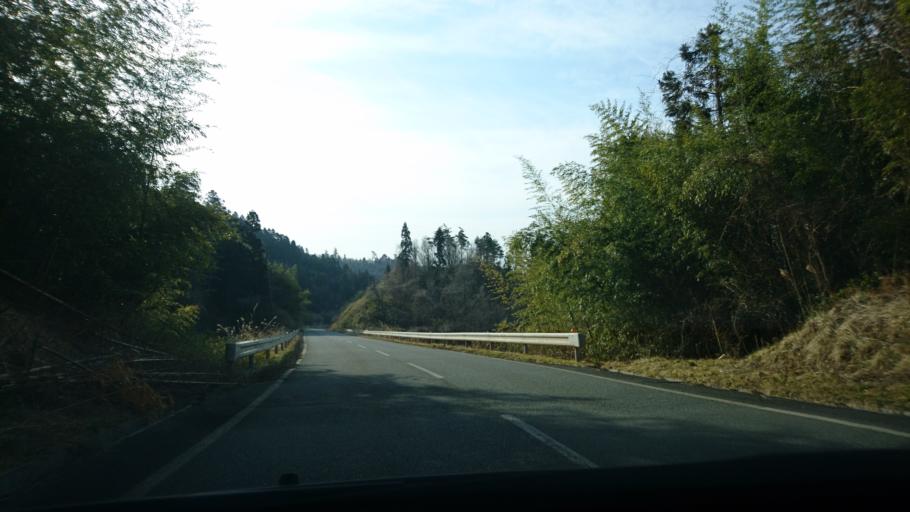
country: JP
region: Iwate
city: Ichinoseki
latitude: 38.8381
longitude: 141.2172
